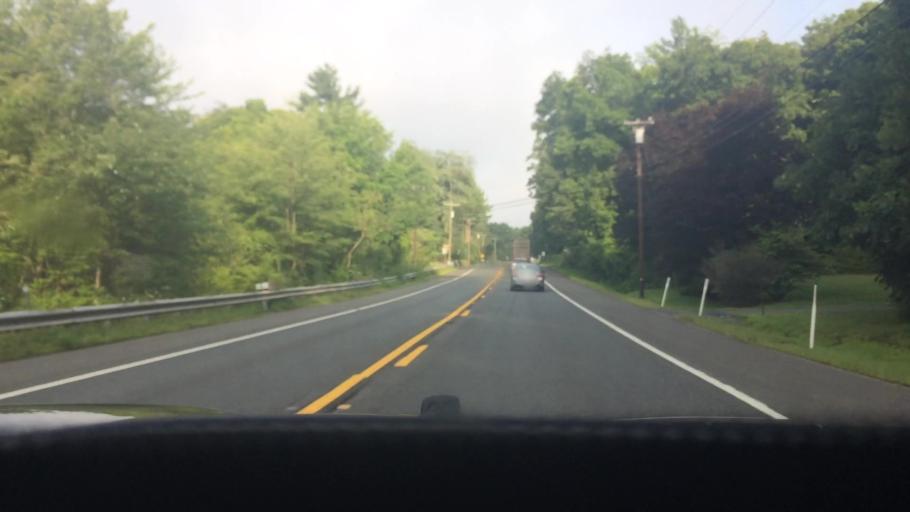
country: US
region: Massachusetts
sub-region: Franklin County
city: Turners Falls
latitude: 42.6087
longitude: -72.5358
